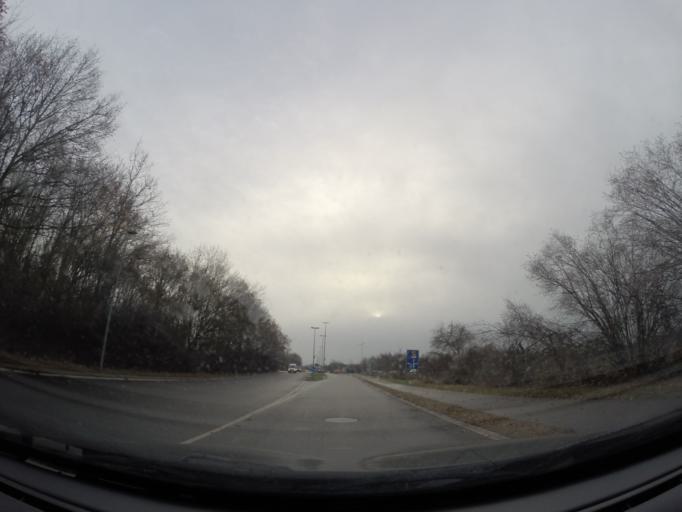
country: DK
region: Capital Region
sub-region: Hoje-Taastrup Kommune
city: Taastrup
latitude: 55.6566
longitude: 12.2675
